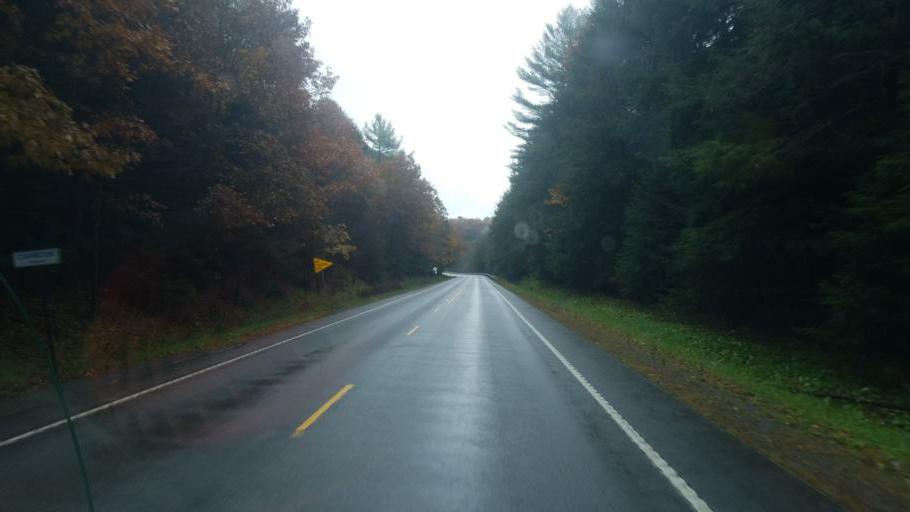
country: US
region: Pennsylvania
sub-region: Clearfield County
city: Shiloh
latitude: 41.1017
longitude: -78.2133
